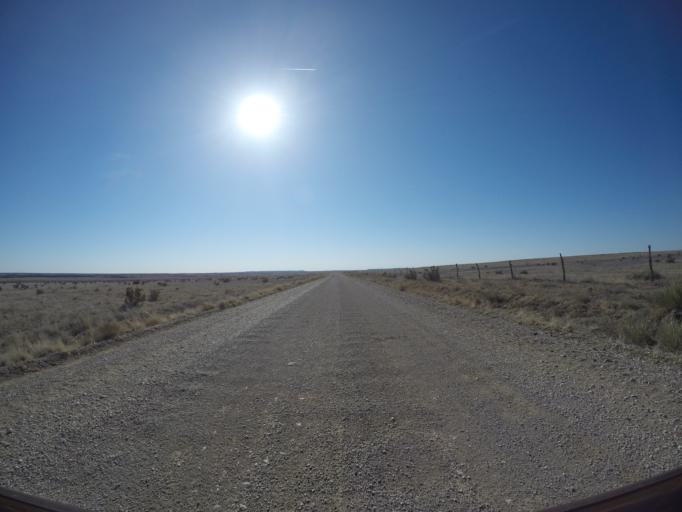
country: US
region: Colorado
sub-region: Otero County
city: La Junta
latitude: 37.7354
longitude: -103.6207
